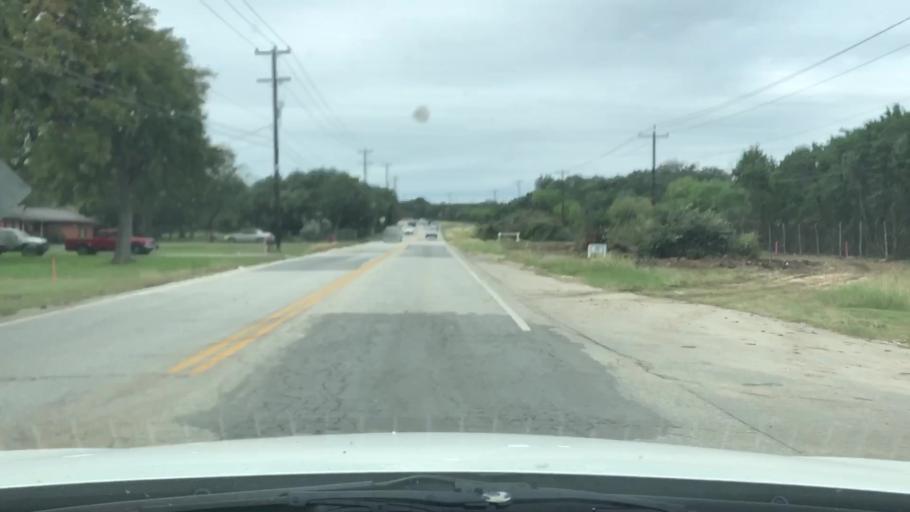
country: US
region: Texas
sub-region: Bexar County
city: Timberwood Park
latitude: 29.6482
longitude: -98.4139
